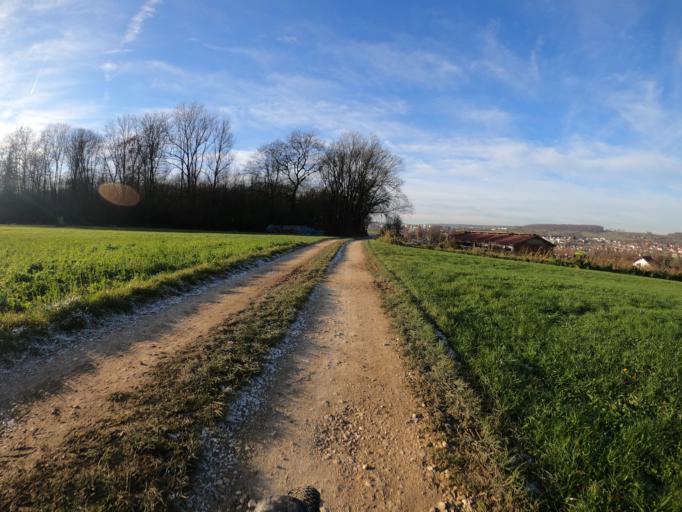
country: DE
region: Baden-Wuerttemberg
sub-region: Regierungsbezirk Stuttgart
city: Goeppingen
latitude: 48.7046
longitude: 9.6318
